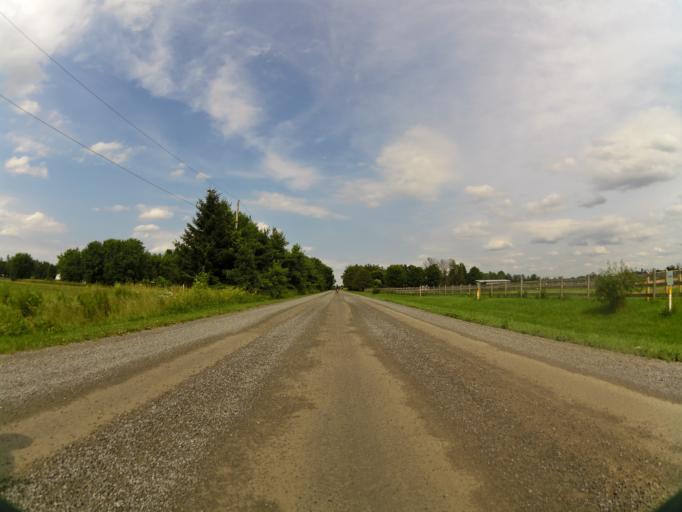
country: CA
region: Ontario
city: Bells Corners
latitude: 45.0956
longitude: -75.5957
